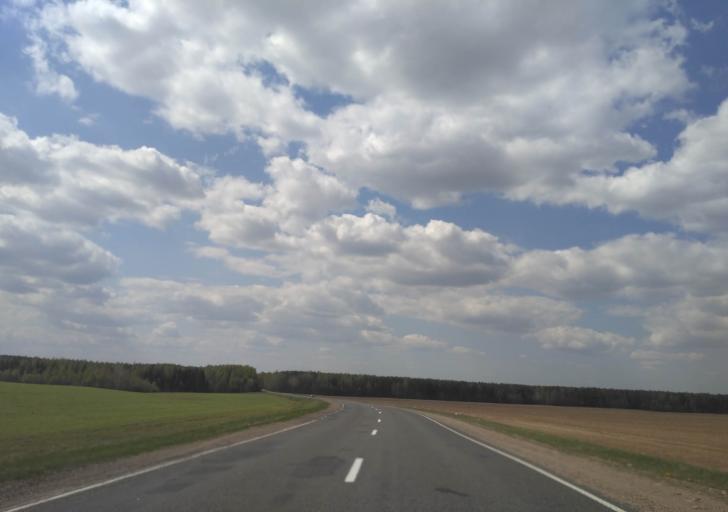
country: BY
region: Minsk
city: Vilyeyka
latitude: 54.5176
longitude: 27.0200
